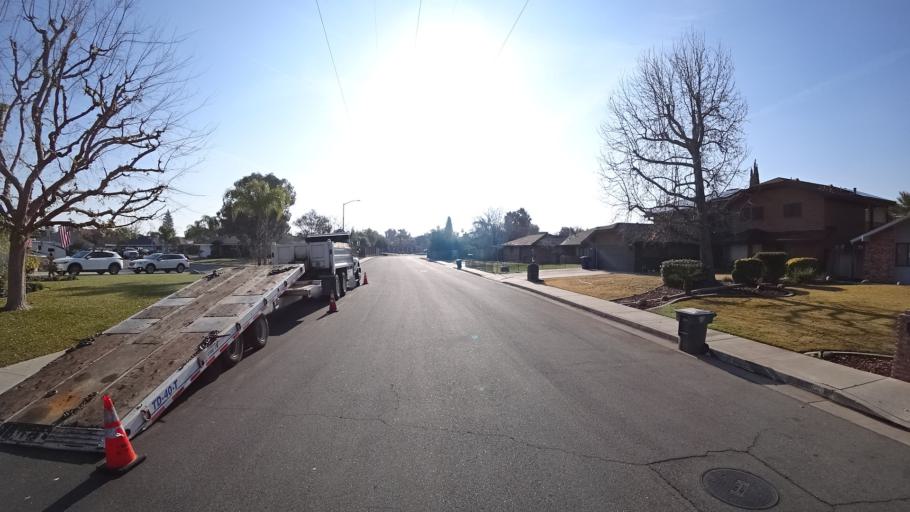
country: US
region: California
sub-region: Kern County
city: Oildale
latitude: 35.4062
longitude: -118.9292
